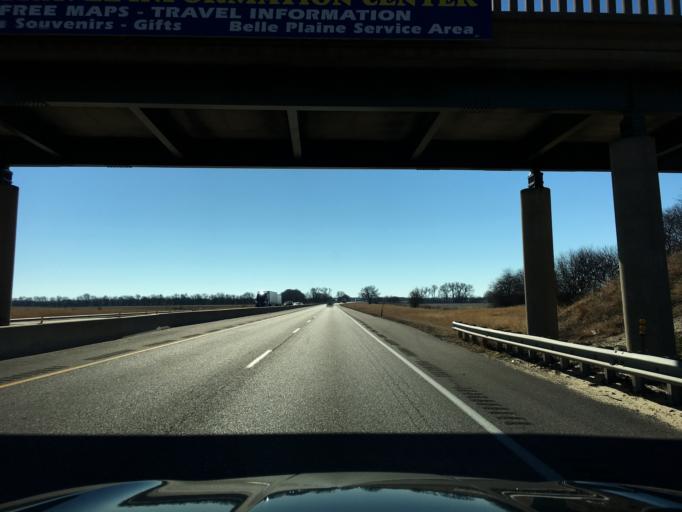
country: US
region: Kansas
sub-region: Sumner County
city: Belle Plaine
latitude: 37.4215
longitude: -97.3213
